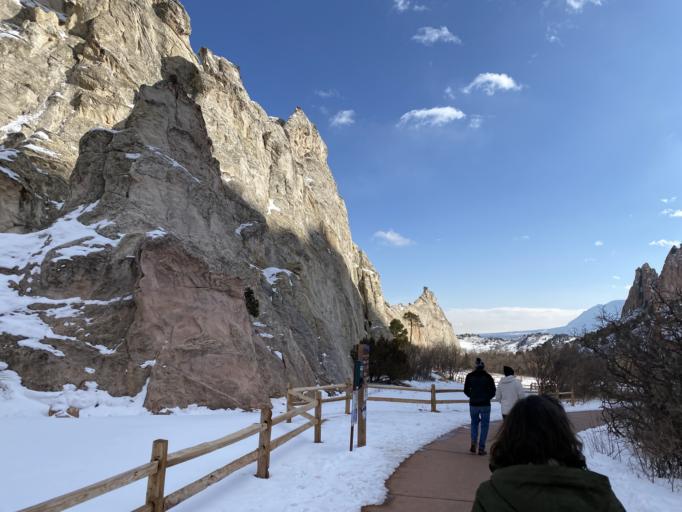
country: US
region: Colorado
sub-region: El Paso County
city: Manitou Springs
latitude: 38.8803
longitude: -104.8799
